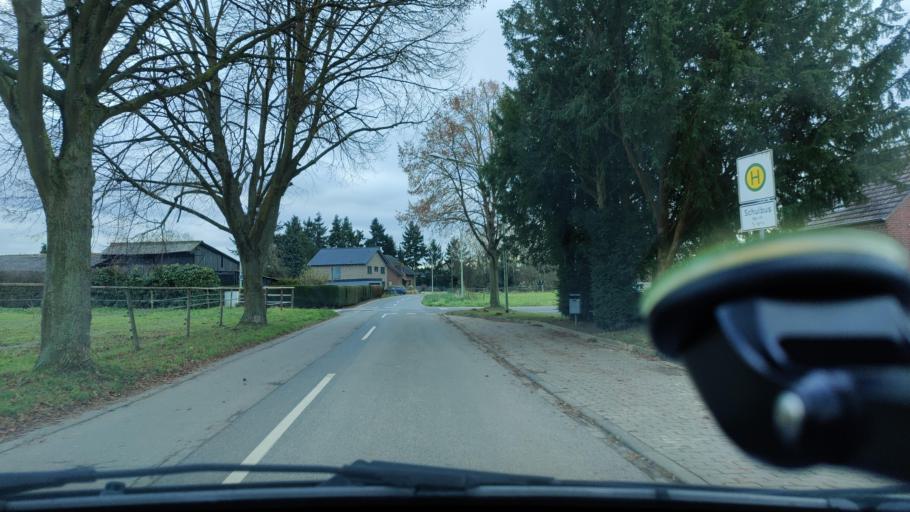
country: DE
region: North Rhine-Westphalia
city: Julich
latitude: 50.9609
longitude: 6.3751
